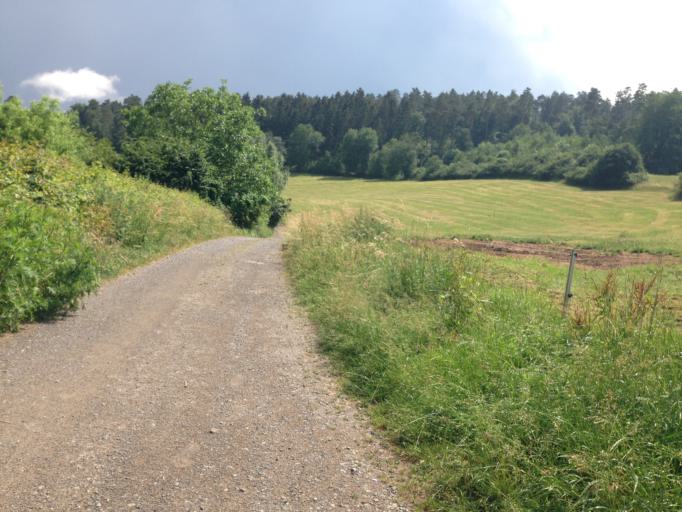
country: DE
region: Hesse
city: Wetter
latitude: 50.8581
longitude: 8.7422
